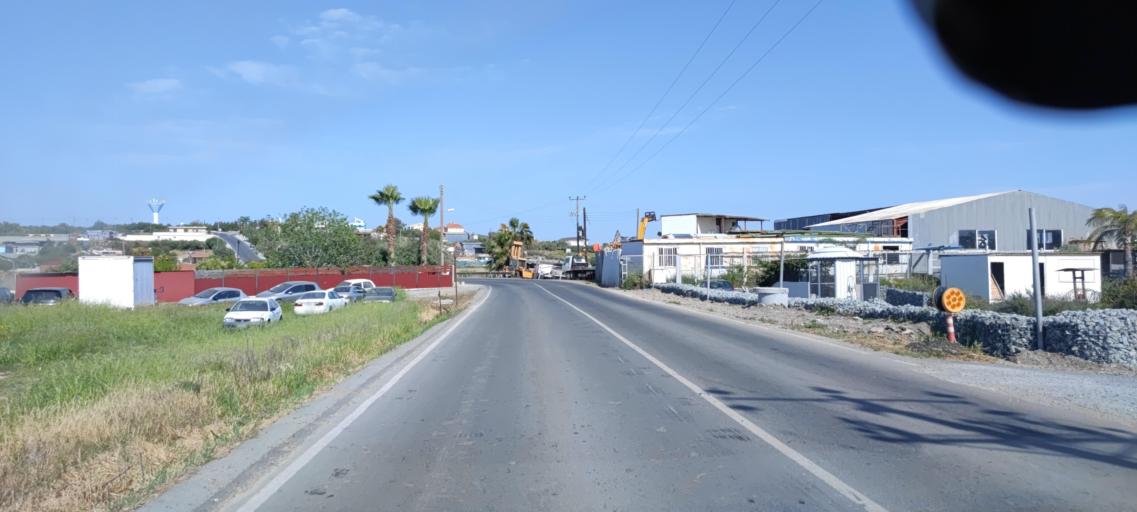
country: CY
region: Larnaka
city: Kolossi
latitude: 34.6559
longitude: 32.9459
